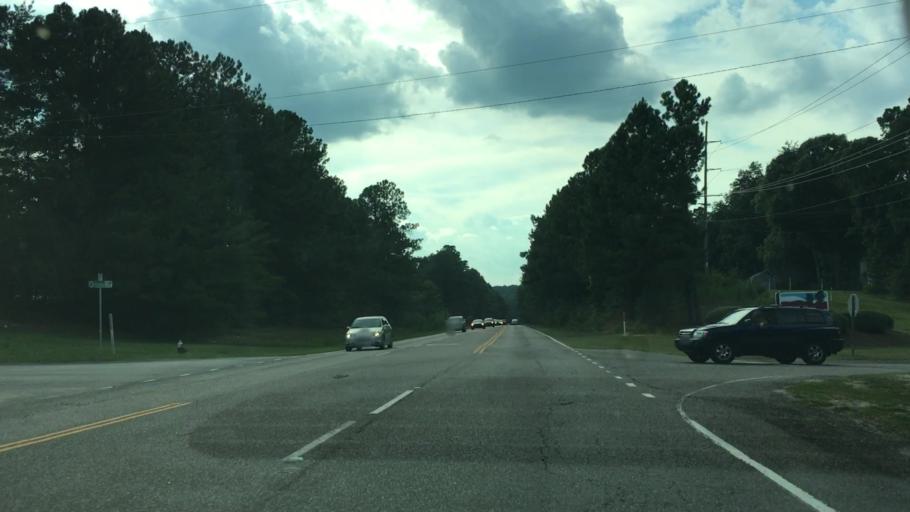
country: US
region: South Carolina
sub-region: Aiken County
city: Aiken
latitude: 33.5249
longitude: -81.7342
